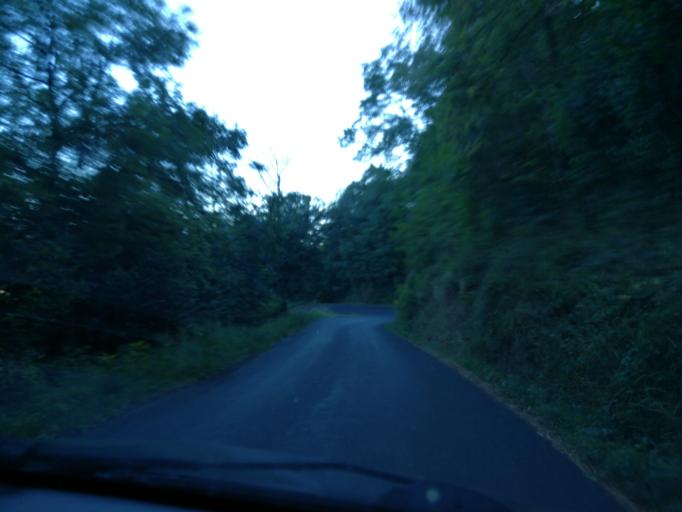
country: FR
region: Auvergne
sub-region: Departement du Cantal
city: Saint-Cernin
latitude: 45.1402
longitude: 2.5043
